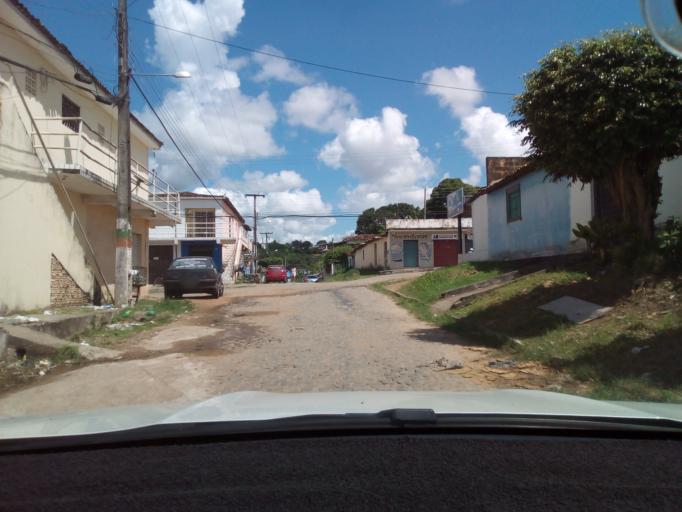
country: BR
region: Paraiba
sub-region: Bayeux
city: Bayeux
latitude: -7.1350
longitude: -34.9318
